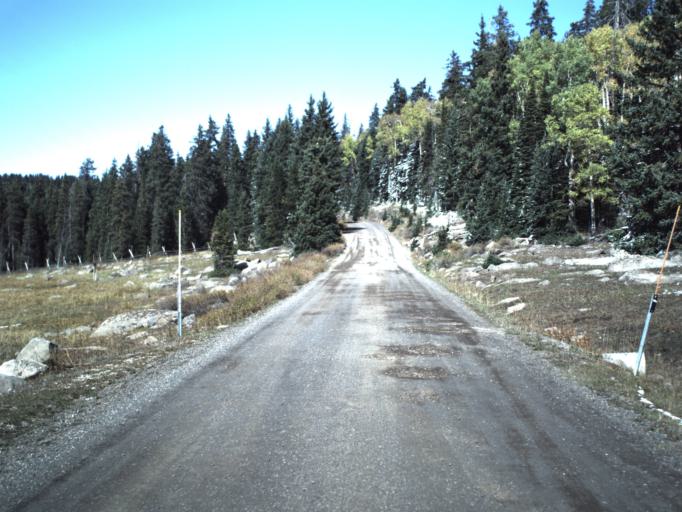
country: US
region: Utah
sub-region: Piute County
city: Junction
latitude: 38.2856
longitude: -112.3578
